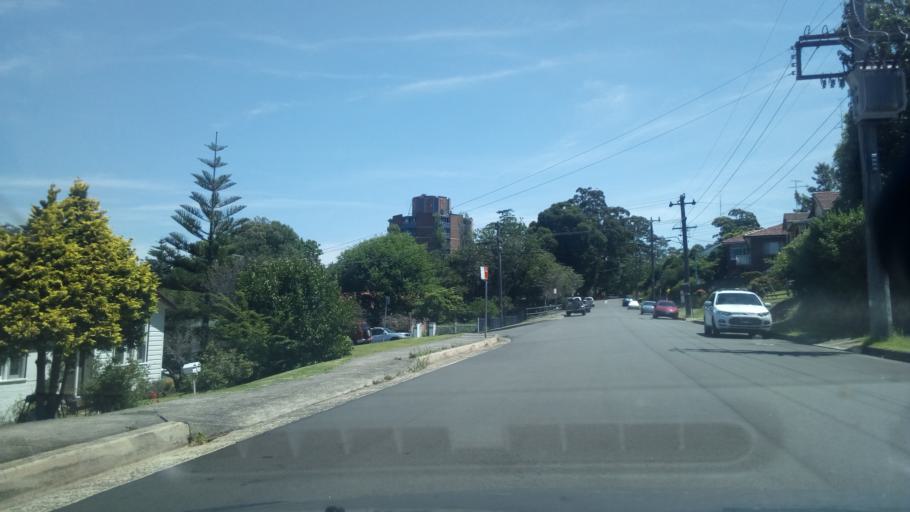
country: AU
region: New South Wales
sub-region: Wollongong
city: Gwynneville
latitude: -34.4268
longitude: 150.8823
